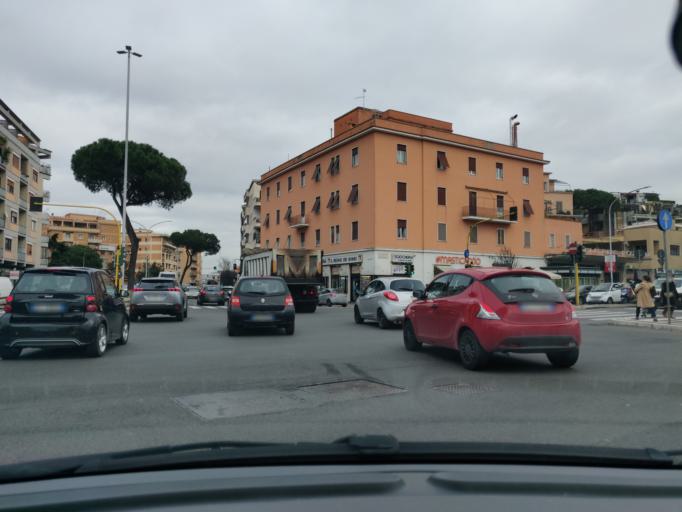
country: VA
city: Vatican City
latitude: 41.8984
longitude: 12.4275
